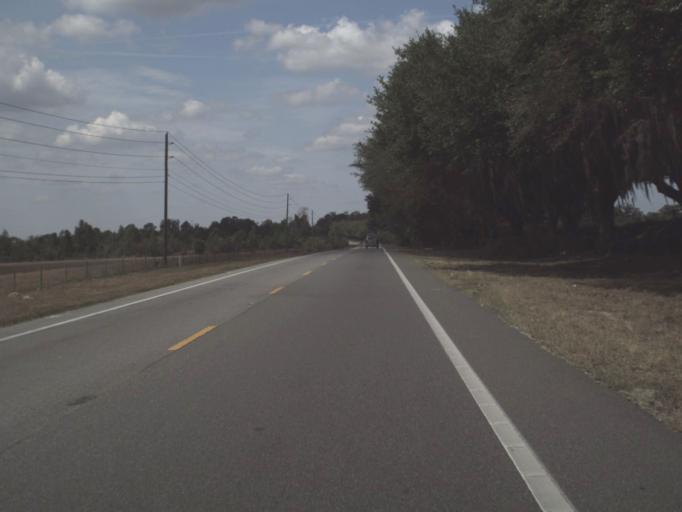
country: US
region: Florida
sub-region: Lake County
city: Mascotte
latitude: 28.5781
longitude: -81.9340
